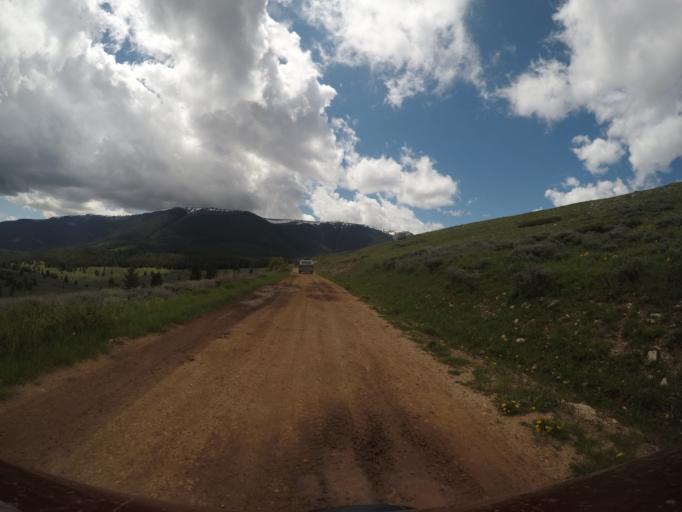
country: US
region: Wyoming
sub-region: Big Horn County
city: Lovell
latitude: 45.1800
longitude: -108.4406
